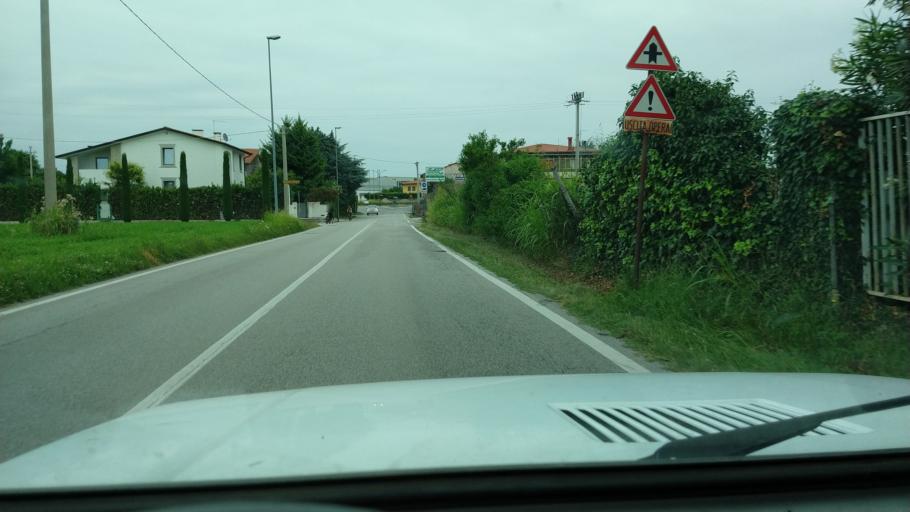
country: IT
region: Veneto
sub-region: Provincia di Vicenza
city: Bassano del Grappa
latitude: 45.7478
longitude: 11.7214
